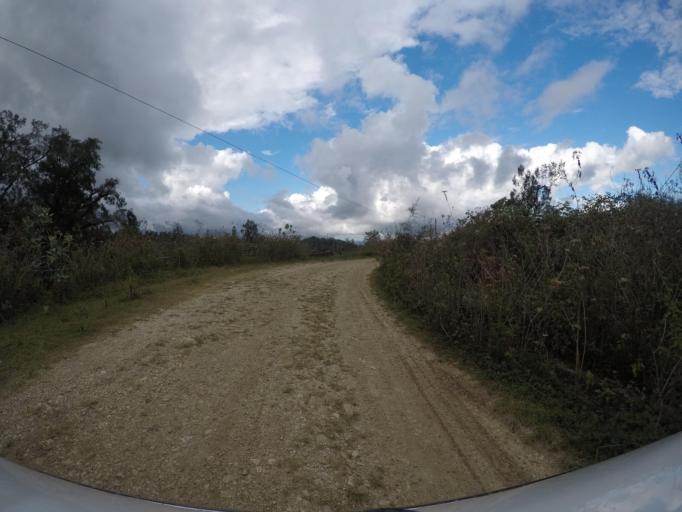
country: TL
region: Baucau
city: Venilale
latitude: -8.6788
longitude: 126.6363
